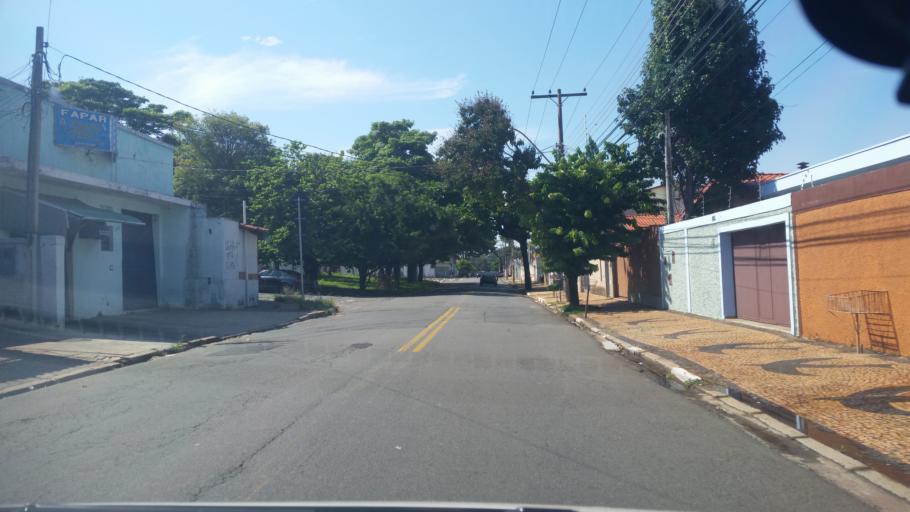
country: BR
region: Sao Paulo
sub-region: Campinas
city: Campinas
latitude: -22.8634
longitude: -47.0665
